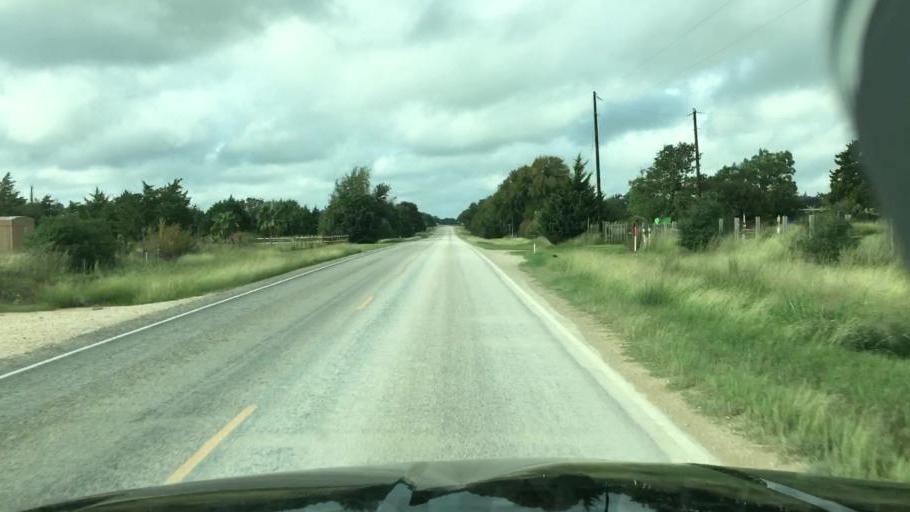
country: US
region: Texas
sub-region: Lee County
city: Giddings
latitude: 30.2668
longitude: -96.8222
